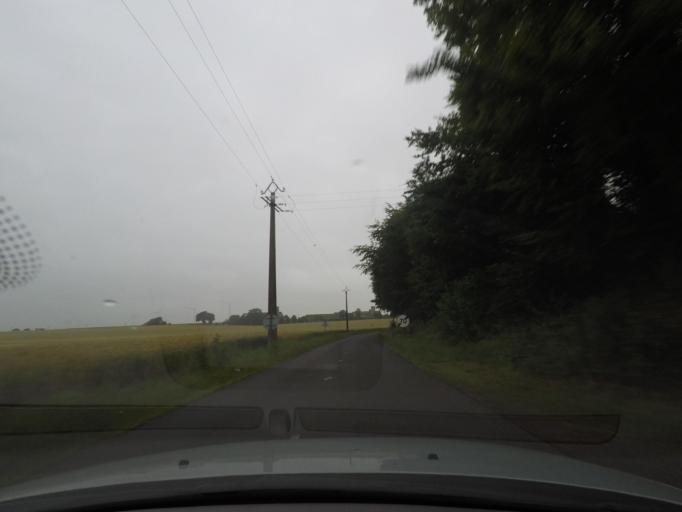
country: FR
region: Haute-Normandie
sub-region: Departement de la Seine-Maritime
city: Saint-Martin-Osmonville
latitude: 49.6140
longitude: 1.2481
